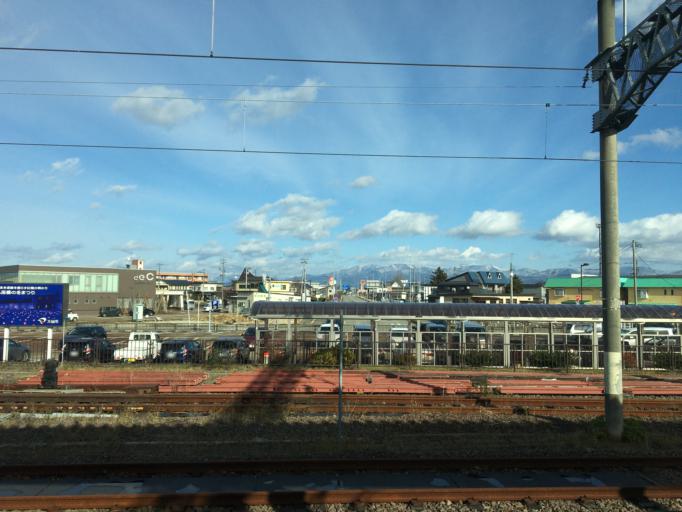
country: JP
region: Akita
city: Omagari
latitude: 39.4664
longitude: 140.4792
